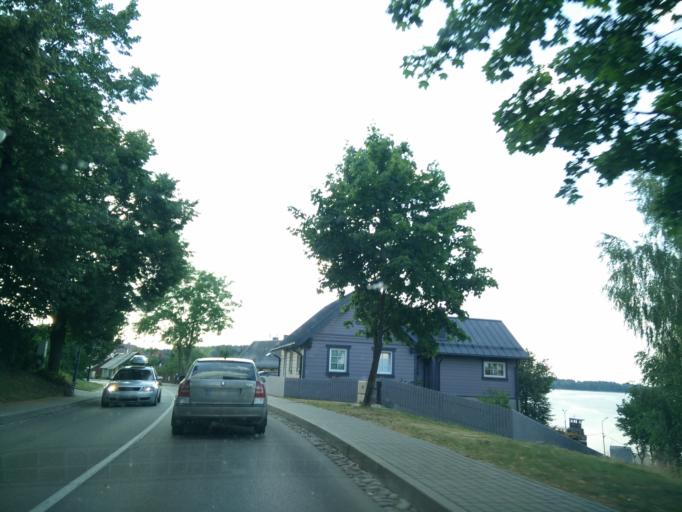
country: LT
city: Trakai
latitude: 54.6520
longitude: 24.9217
